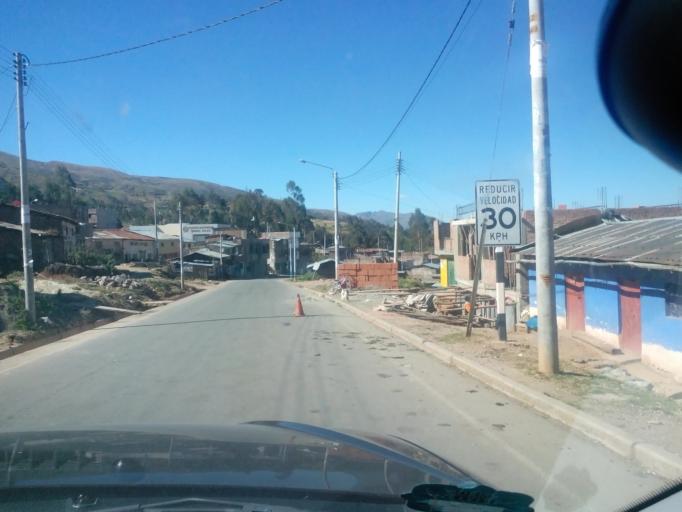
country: PE
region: Apurimac
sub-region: Provincia de Andahuaylas
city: Talavera
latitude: -13.6533
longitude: -73.5320
